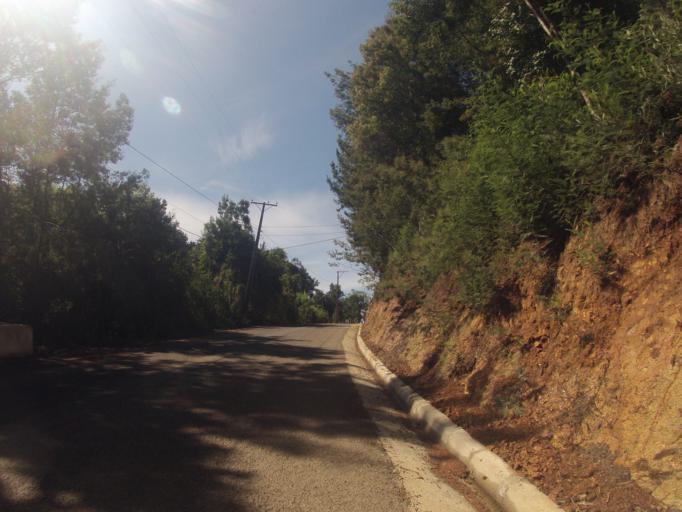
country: CL
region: Araucania
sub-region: Provincia de Cautin
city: Temuco
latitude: -38.6846
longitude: -72.5609
